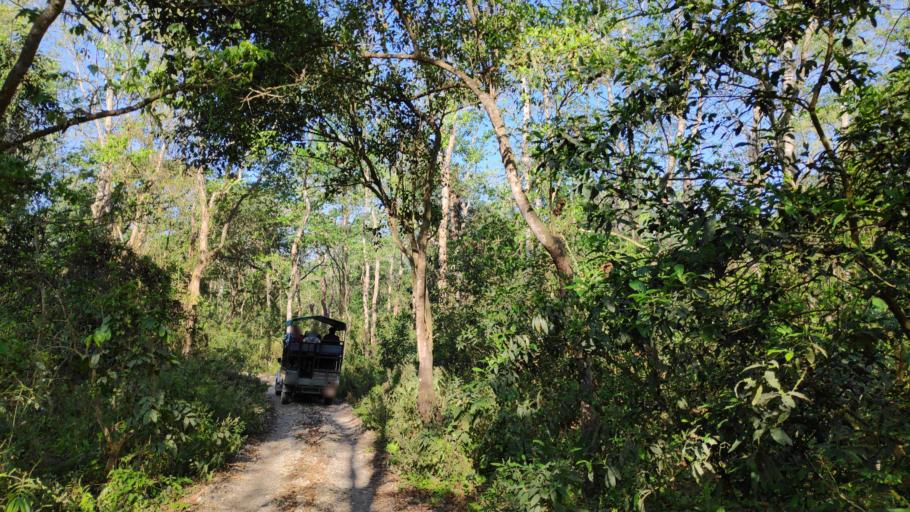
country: NP
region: Central Region
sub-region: Narayani Zone
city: Bharatpur
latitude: 27.5621
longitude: 84.5371
